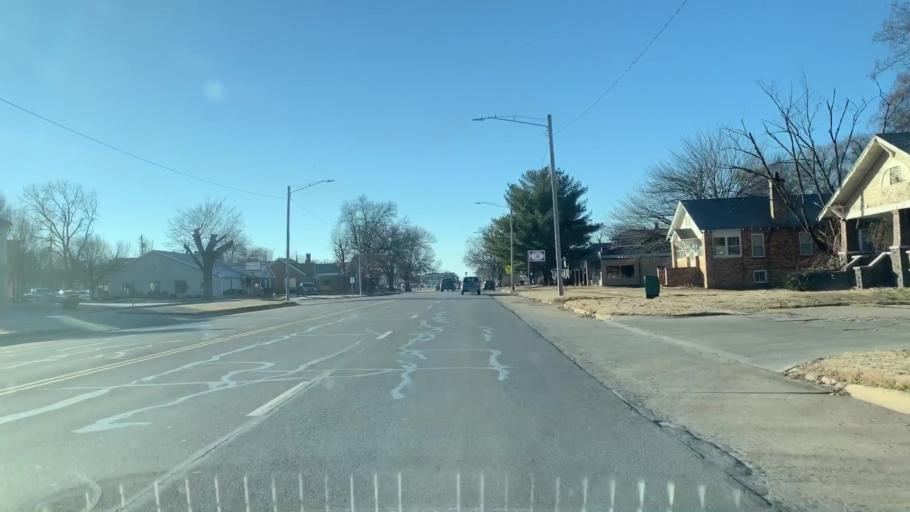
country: US
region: Kansas
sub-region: Crawford County
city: Pittsburg
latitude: 37.4228
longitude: -94.7050
